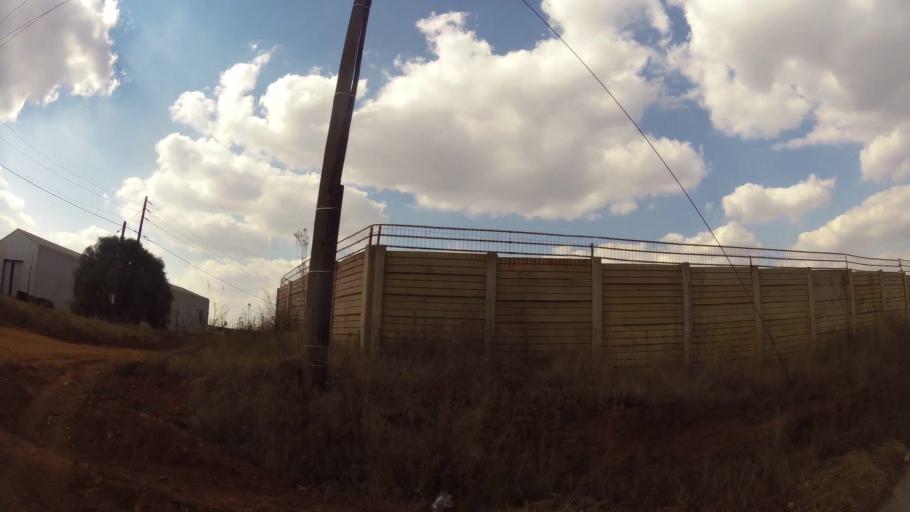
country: ZA
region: Mpumalanga
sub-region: Nkangala District Municipality
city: Delmas
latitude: -26.1326
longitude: 28.6783
